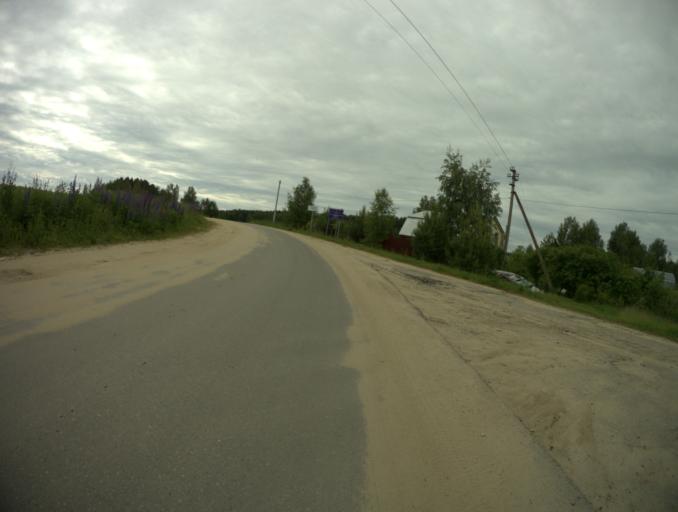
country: RU
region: Vladimir
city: Kommunar
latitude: 56.0500
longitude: 40.4814
